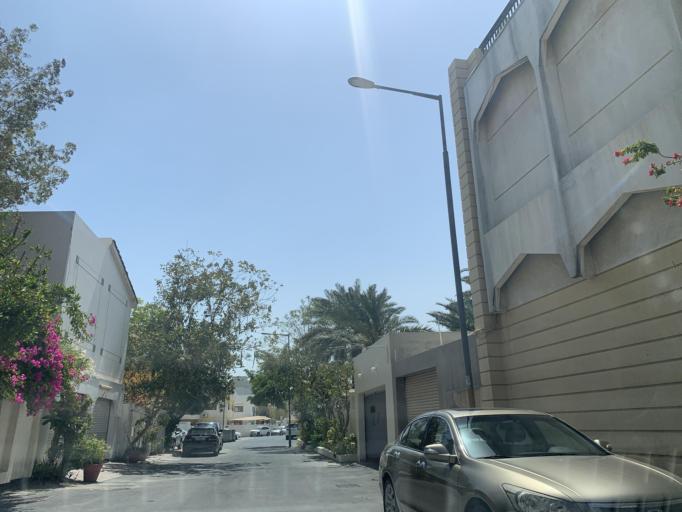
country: BH
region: Manama
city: Manama
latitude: 26.2124
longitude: 50.5821
